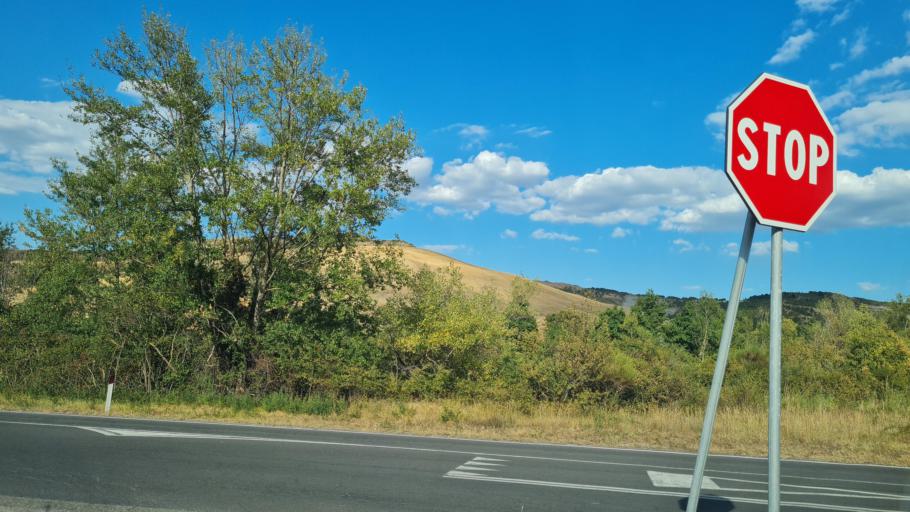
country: IT
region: Tuscany
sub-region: Provincia di Siena
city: Abbadia San Salvatore
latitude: 42.9410
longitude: 11.7108
